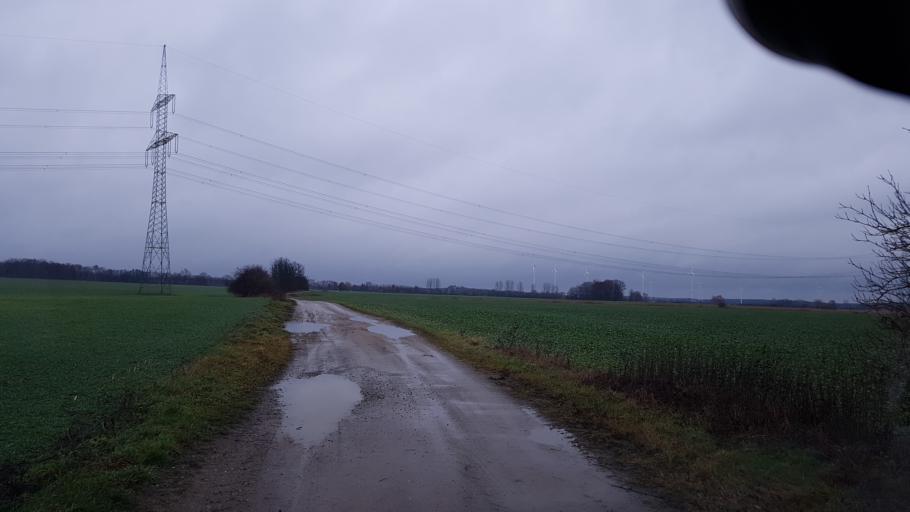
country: DE
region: Brandenburg
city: Sallgast
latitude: 51.6257
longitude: 13.8459
